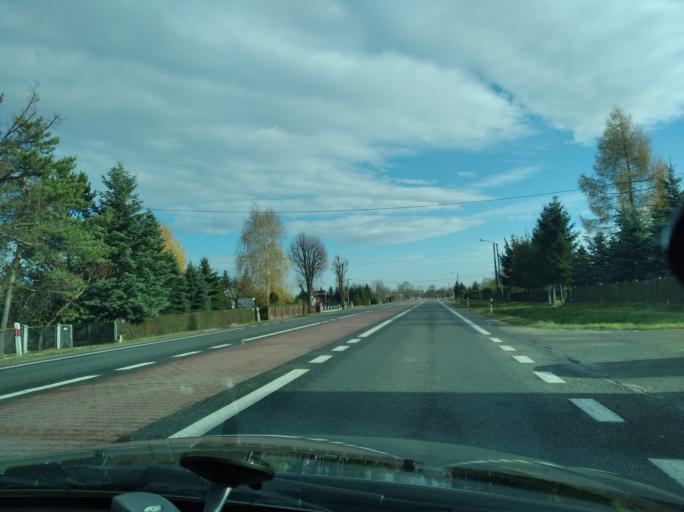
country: PL
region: Subcarpathian Voivodeship
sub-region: Powiat debicki
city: Brzeznica
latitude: 50.0621
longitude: 21.5048
